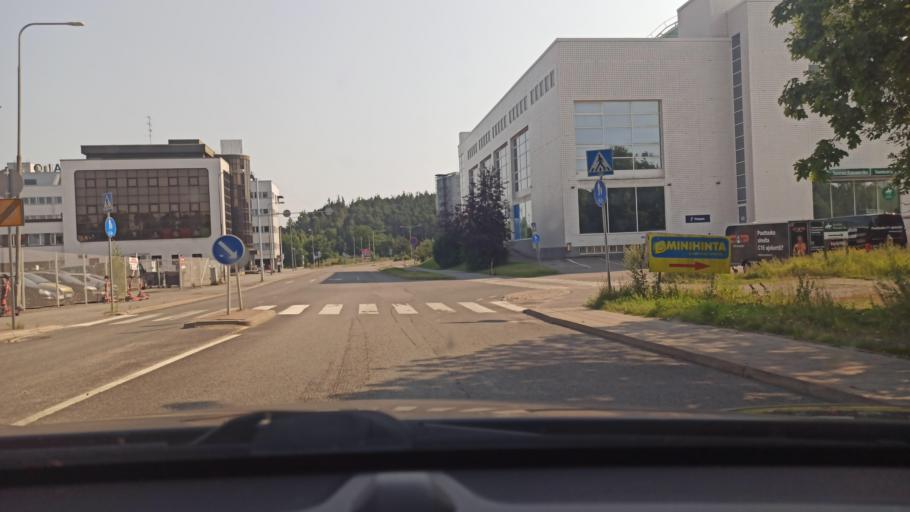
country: FI
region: Varsinais-Suomi
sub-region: Turku
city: Turku
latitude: 60.4587
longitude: 22.2355
